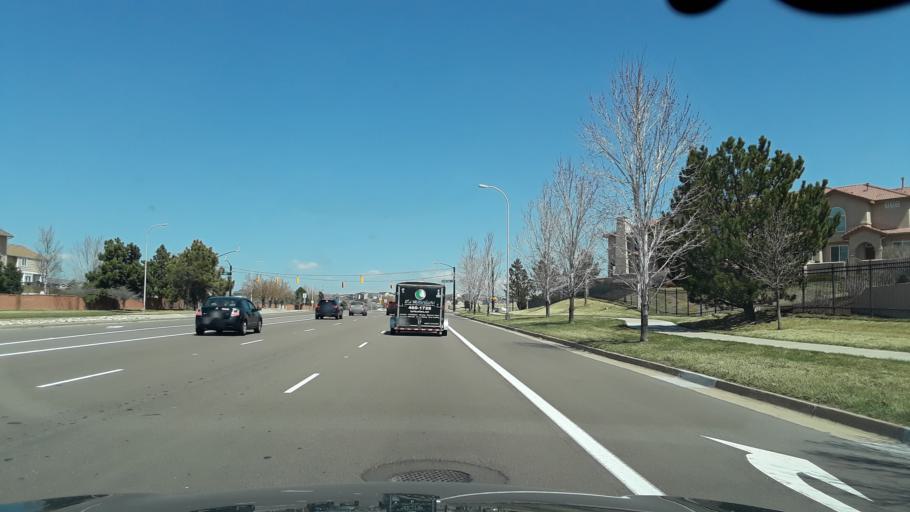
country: US
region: Colorado
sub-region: El Paso County
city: Cimarron Hills
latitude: 38.9345
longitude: -104.7405
